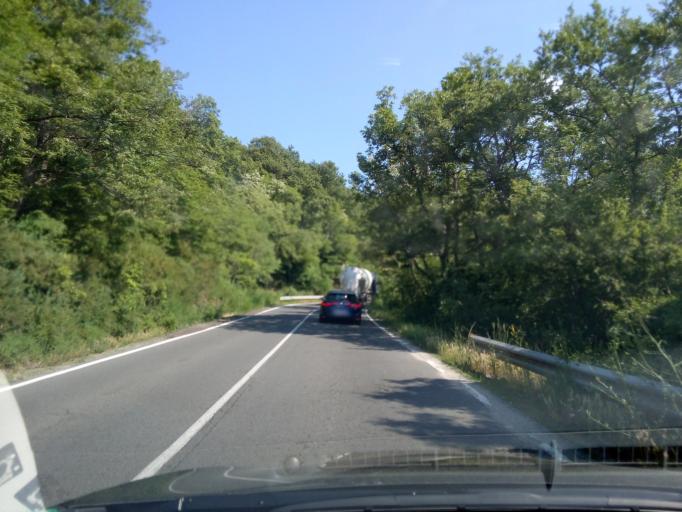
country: BG
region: Burgas
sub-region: Obshtina Nesebur
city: Sveti Vlas
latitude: 42.7342
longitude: 27.7387
